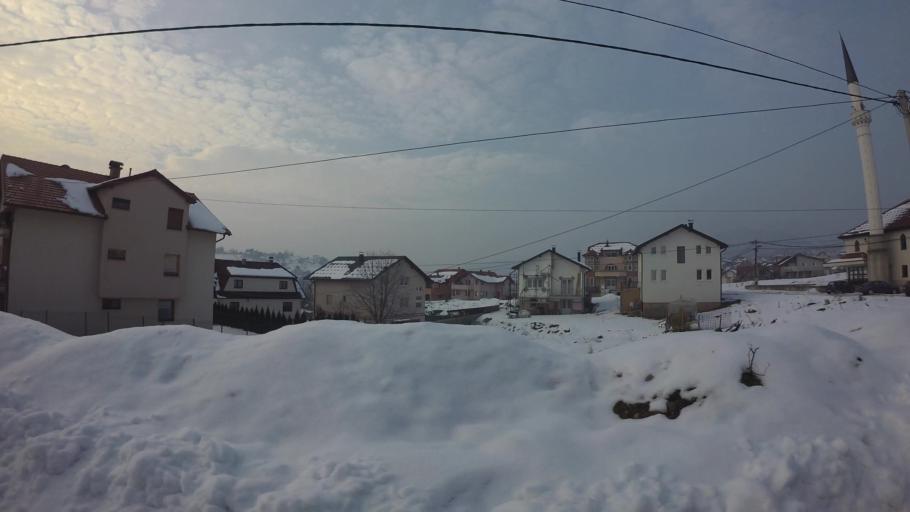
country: BA
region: Federation of Bosnia and Herzegovina
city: Hotonj
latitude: 43.8923
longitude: 18.3782
